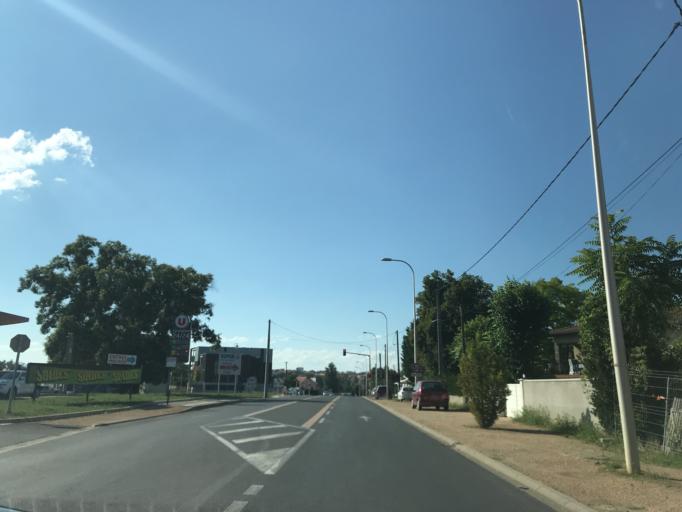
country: FR
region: Auvergne
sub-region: Departement du Puy-de-Dome
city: Pont-du-Chateau
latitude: 45.7911
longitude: 3.2627
